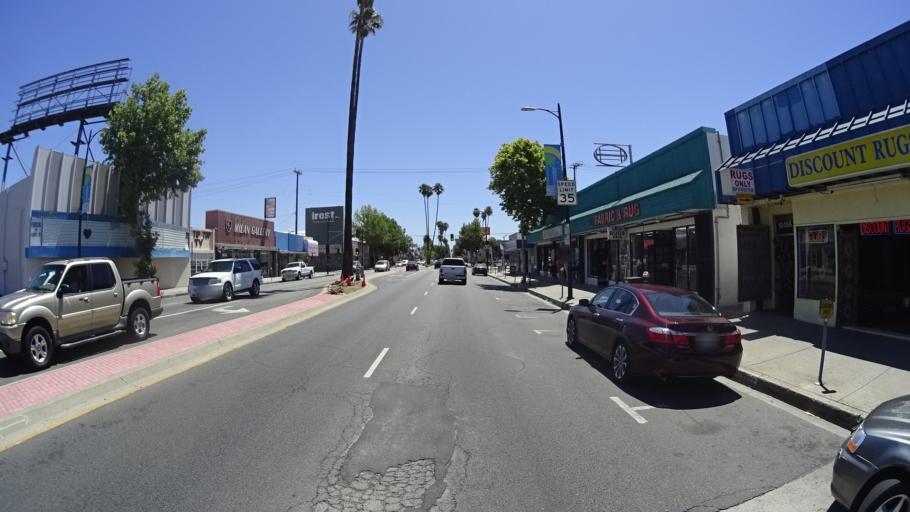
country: US
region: California
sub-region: Los Angeles County
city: Northridge
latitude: 34.2011
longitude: -118.5357
